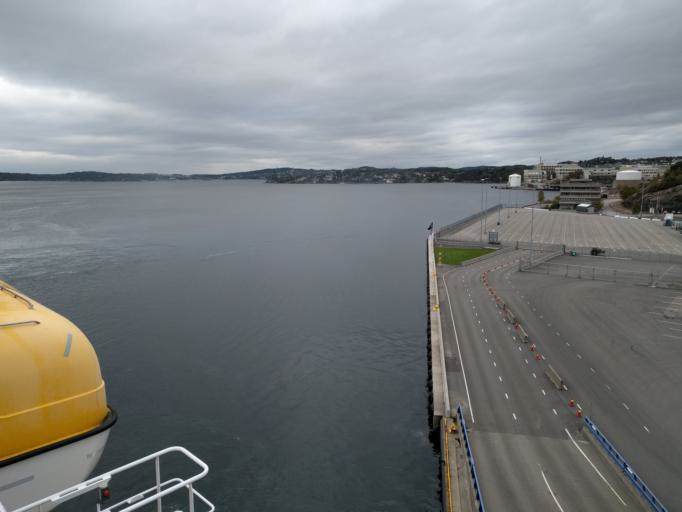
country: NO
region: Vest-Agder
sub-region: Kristiansand
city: Kristiansand
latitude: 58.1436
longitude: 7.9854
